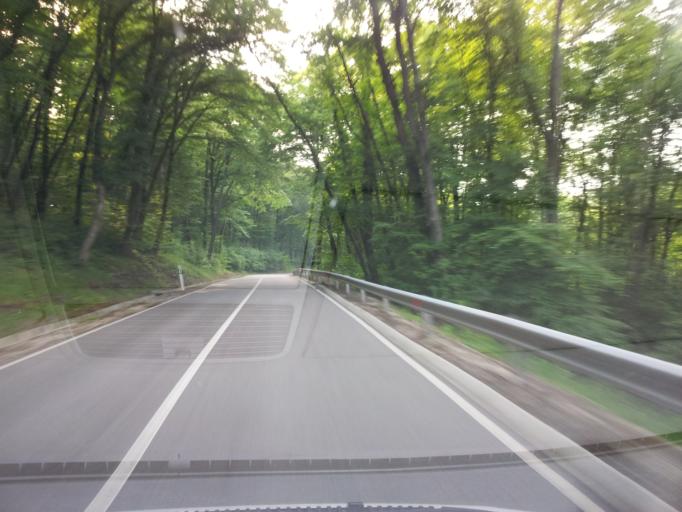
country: HU
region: Komarom-Esztergom
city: Kesztolc
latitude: 47.7322
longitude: 18.8285
